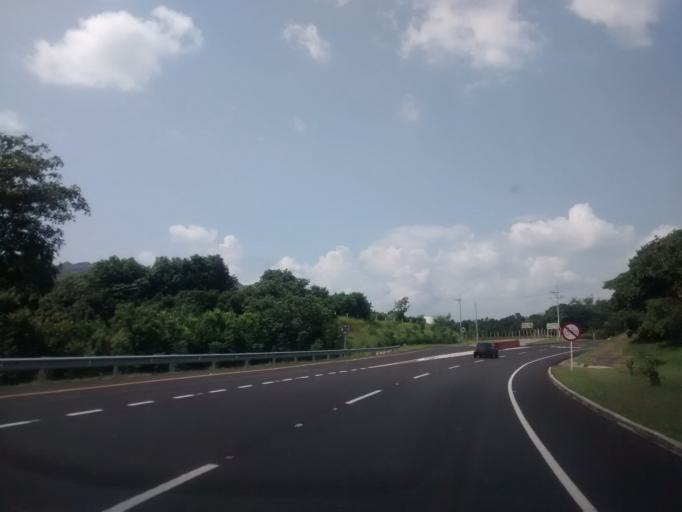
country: CO
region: Tolima
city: Valle de San Juan
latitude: 4.2779
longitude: -75.0123
